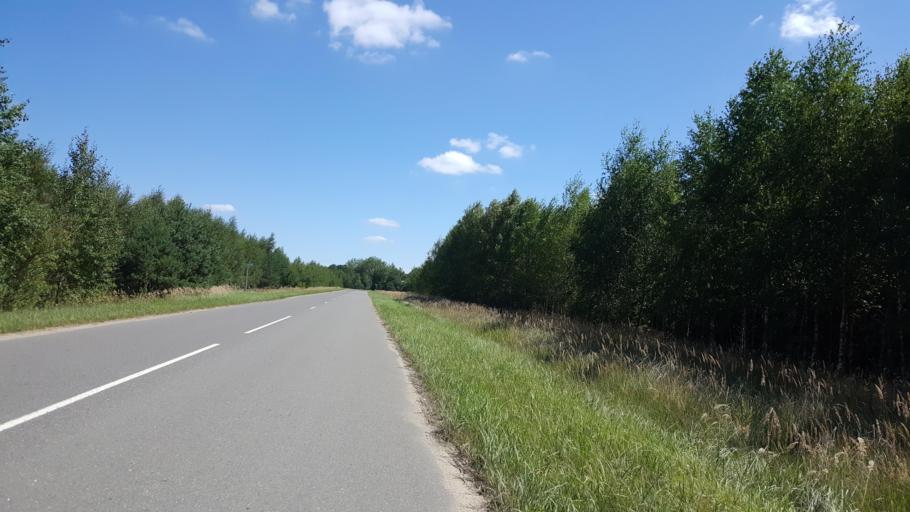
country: BY
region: Brest
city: Kobryn
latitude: 52.3491
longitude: 24.3279
